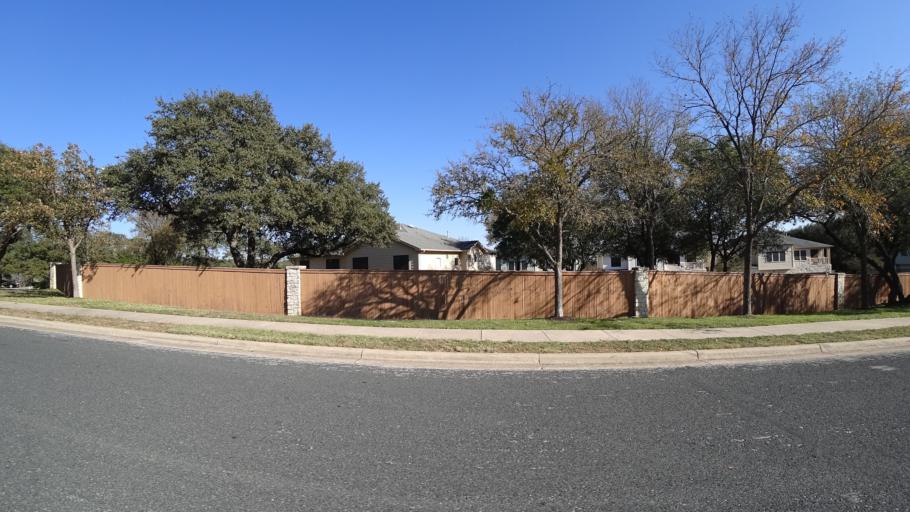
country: US
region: Texas
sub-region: Travis County
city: Barton Creek
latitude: 30.2275
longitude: -97.8745
